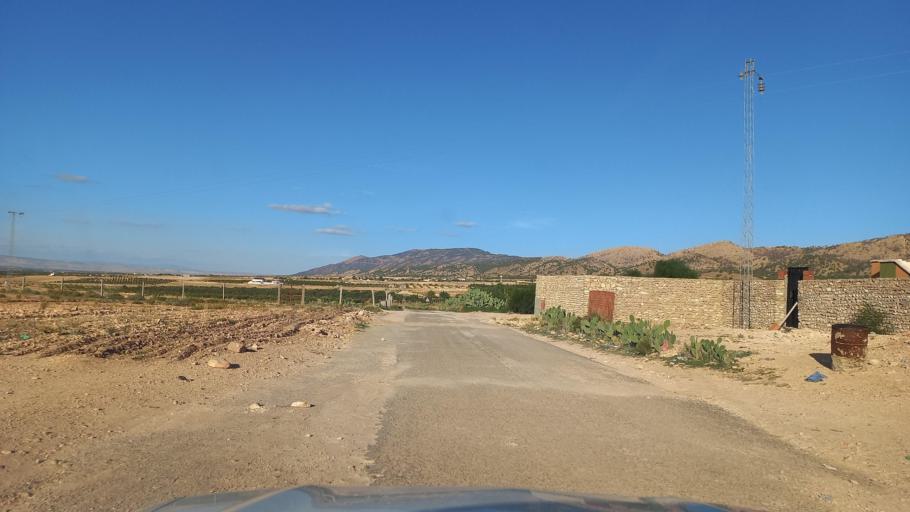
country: TN
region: Al Qasrayn
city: Sbiba
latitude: 35.3564
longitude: 9.1383
